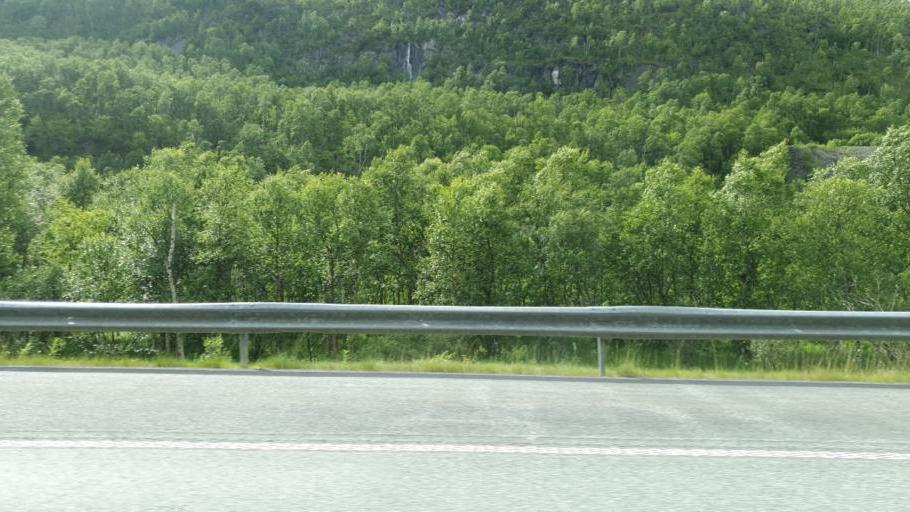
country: NO
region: Sor-Trondelag
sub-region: Oppdal
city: Oppdal
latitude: 62.3695
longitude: 9.6371
